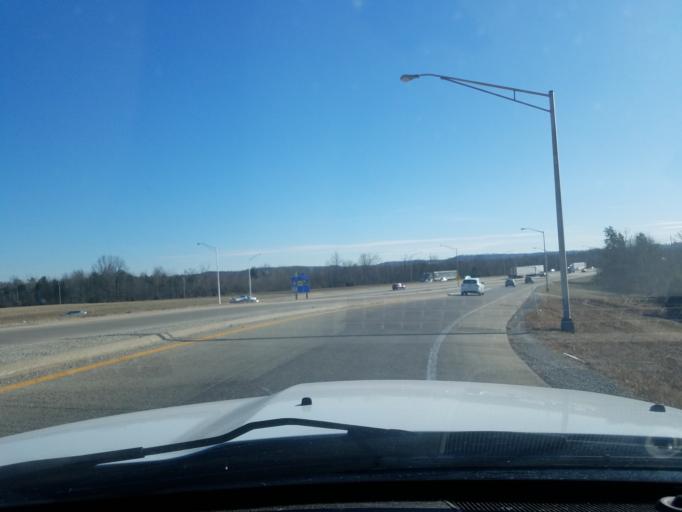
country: US
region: Kentucky
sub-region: Bullitt County
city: Shepherdsville
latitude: 37.9915
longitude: -85.7048
